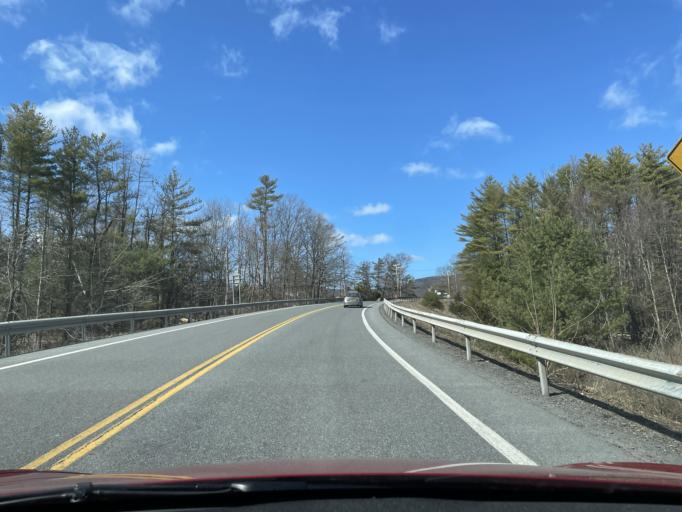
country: US
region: New York
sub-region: Ulster County
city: Woodstock
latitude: 42.0219
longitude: -74.1060
